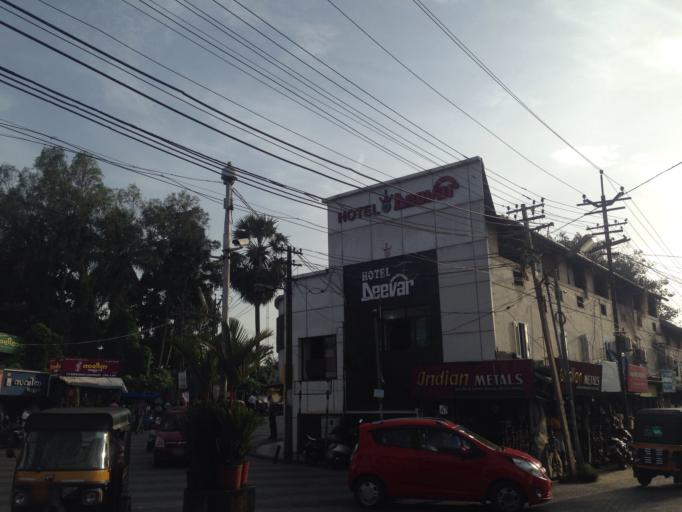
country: IN
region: Kerala
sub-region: Kozhikode
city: Kozhikode
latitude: 11.2489
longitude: 75.7814
